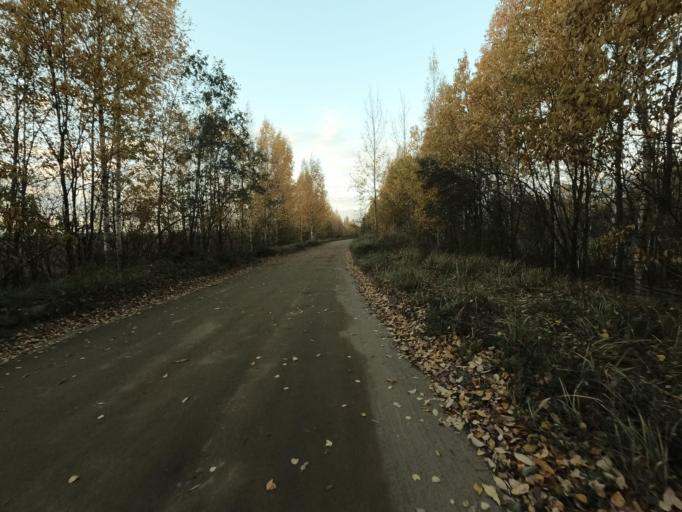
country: RU
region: Leningrad
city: Mga
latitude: 59.7961
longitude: 31.2003
